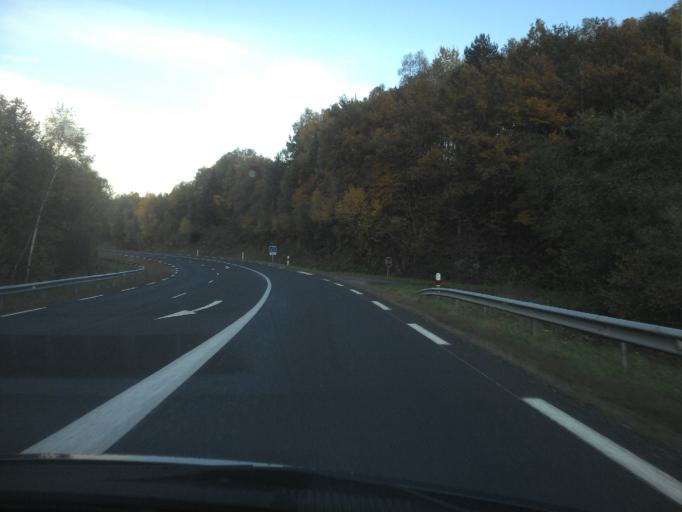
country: FR
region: Auvergne
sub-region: Departement du Puy-de-Dome
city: Gelles
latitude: 45.8359
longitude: 2.7346
